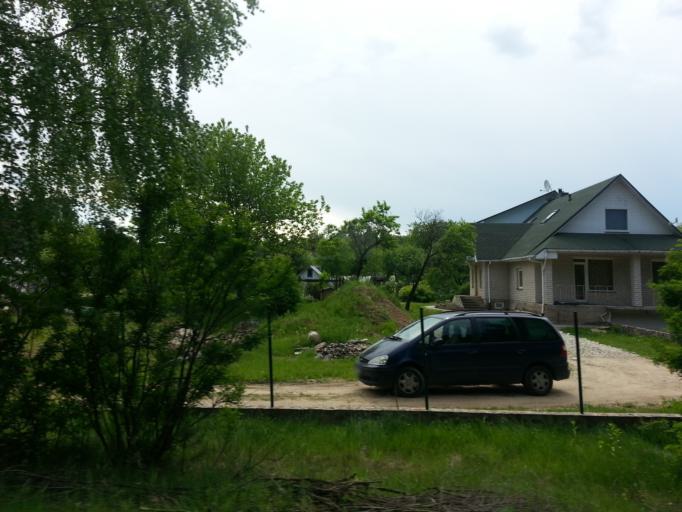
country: LT
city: Grigiskes
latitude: 54.7551
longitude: 25.0731
